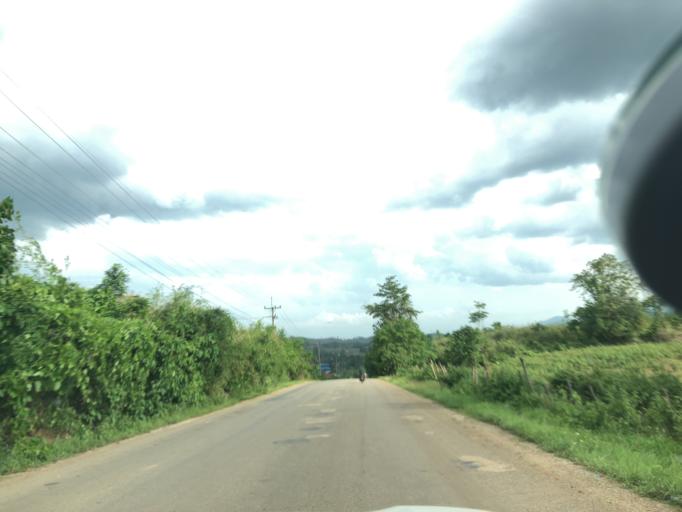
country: TH
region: Uttaradit
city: Ban Khok
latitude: 18.1211
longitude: 101.3728
